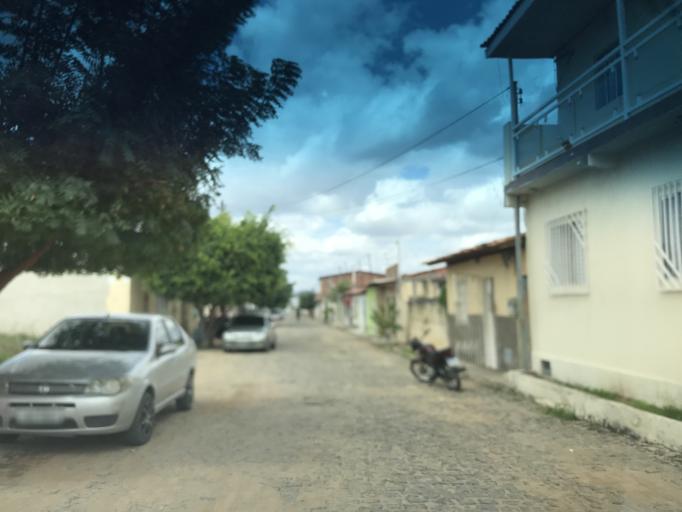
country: BR
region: Bahia
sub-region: Itaberaba
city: Itaberaba
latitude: -12.5350
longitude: -40.3037
